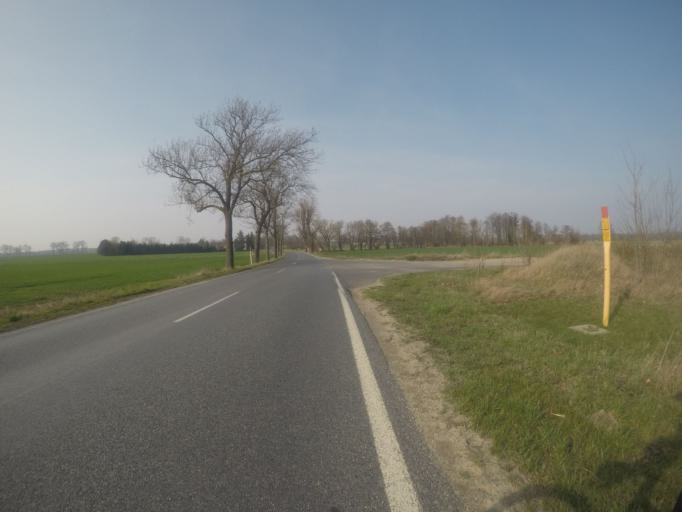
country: DE
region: Brandenburg
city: Schonefeld
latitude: 52.3308
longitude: 13.5018
